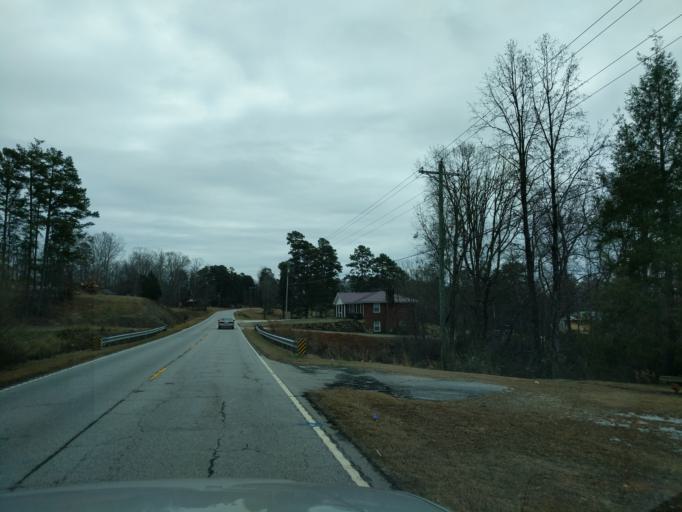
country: US
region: South Carolina
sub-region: Oconee County
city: Westminster
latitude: 34.7136
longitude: -83.2005
